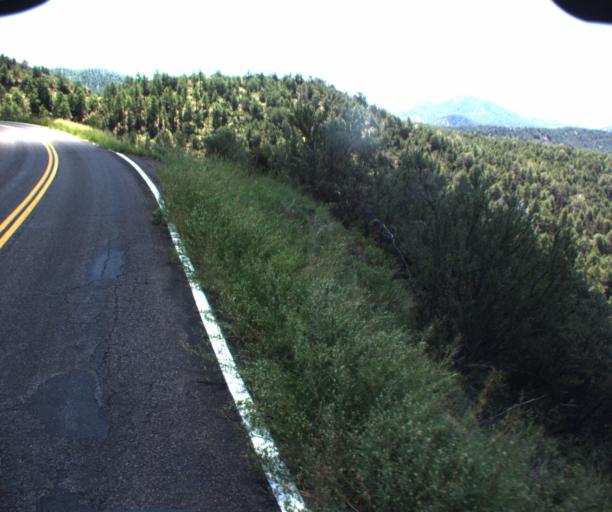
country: US
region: Arizona
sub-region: Greenlee County
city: Morenci
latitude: 33.2174
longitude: -109.3816
